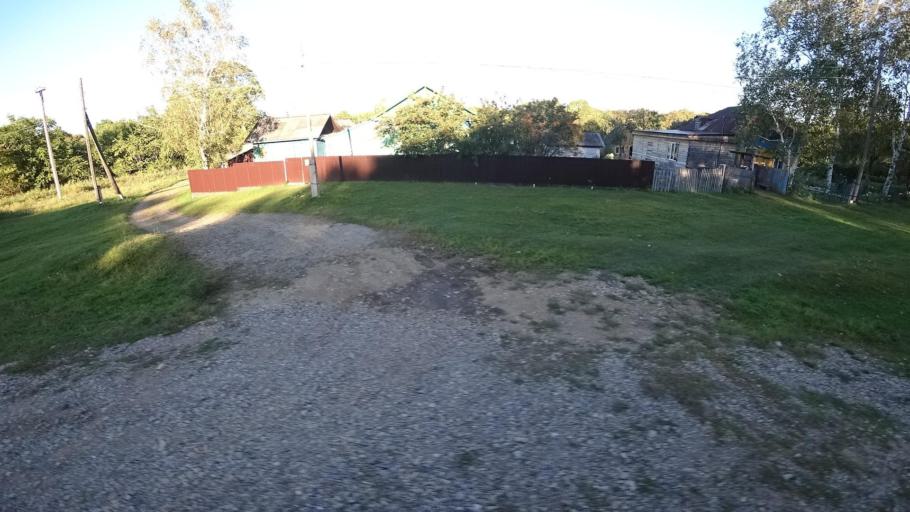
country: RU
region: Primorskiy
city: Kirovskiy
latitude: 44.8289
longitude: 133.5751
